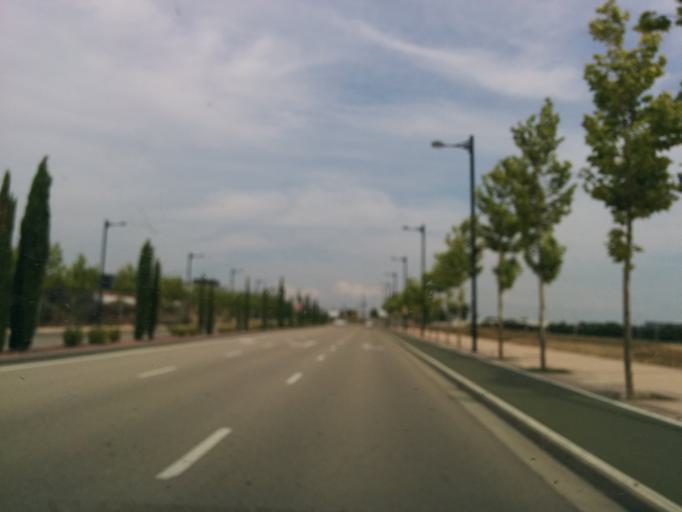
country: ES
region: Aragon
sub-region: Provincia de Zaragoza
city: Almozara
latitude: 41.6871
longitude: -0.8926
